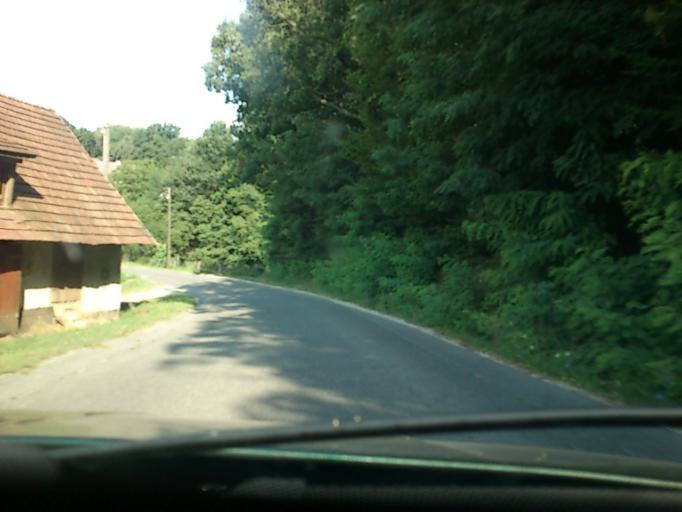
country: SI
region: Duplek
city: Spodnji Duplek
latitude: 46.5349
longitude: 15.7626
